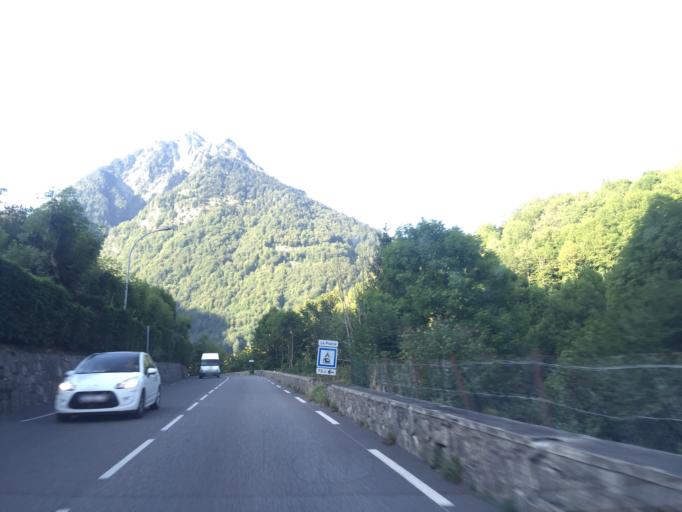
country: FR
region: Midi-Pyrenees
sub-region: Departement des Hautes-Pyrenees
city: Cauterets
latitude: 42.8971
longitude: -0.1118
